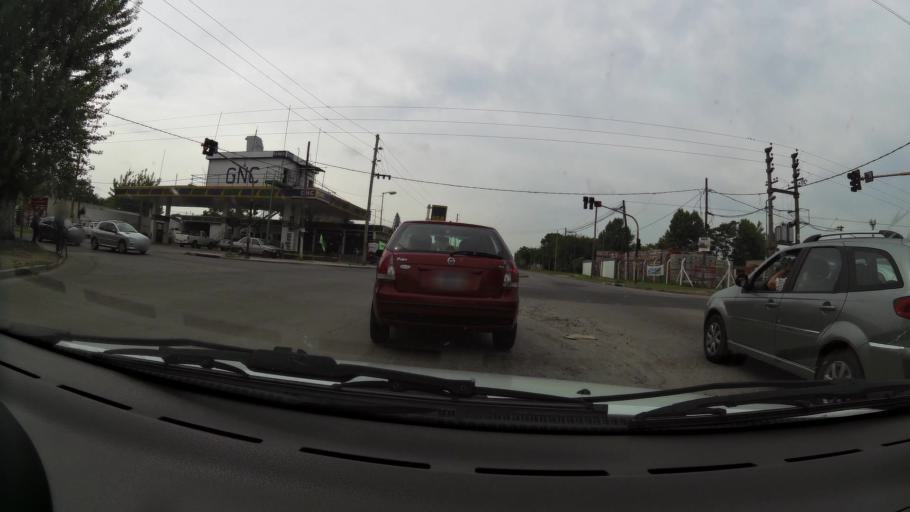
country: AR
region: Buenos Aires
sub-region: Partido de La Plata
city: La Plata
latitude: -34.9346
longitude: -58.0065
